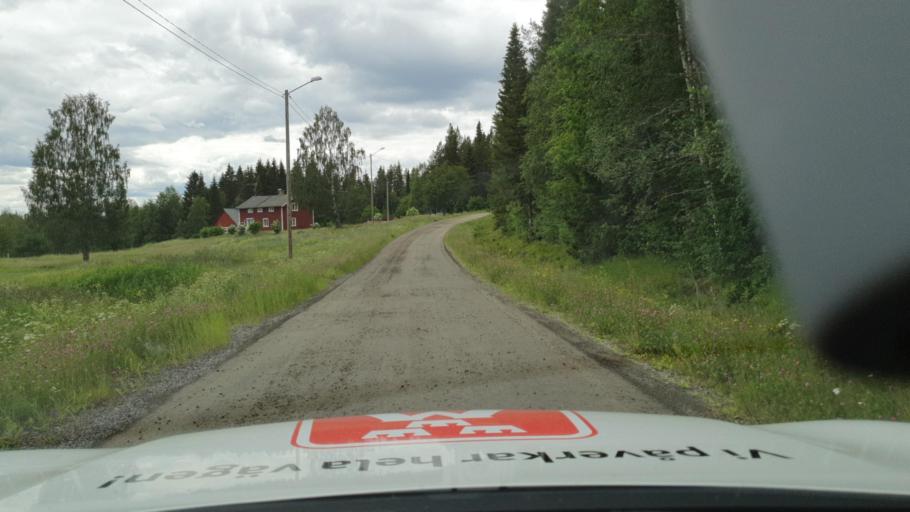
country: SE
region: Vaesterbotten
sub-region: Bjurholms Kommun
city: Bjurholm
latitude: 63.8125
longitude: 19.0425
